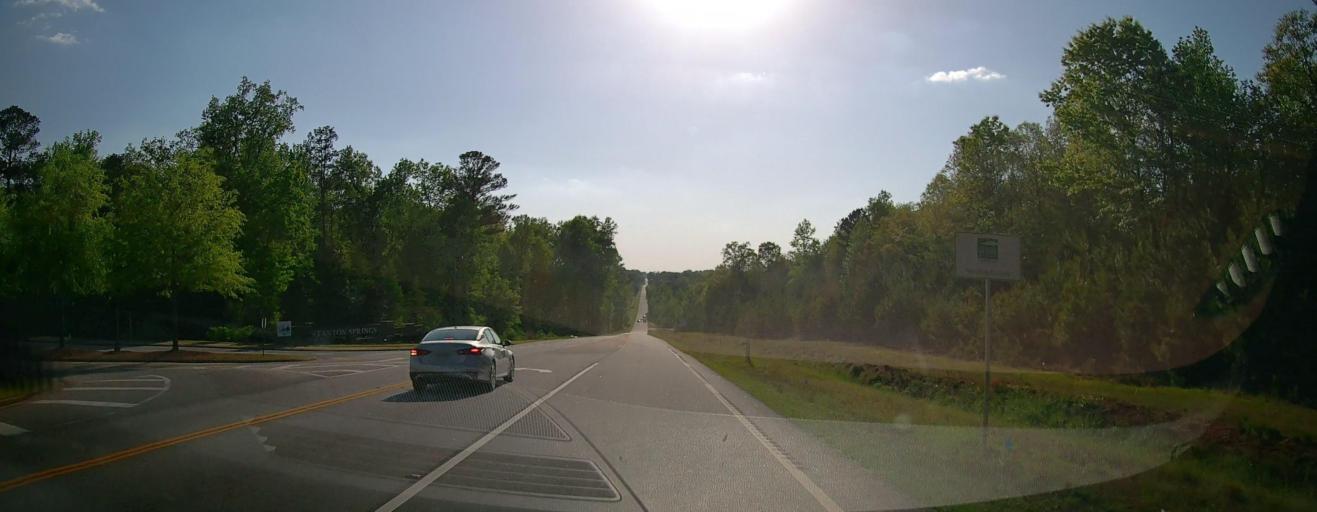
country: US
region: Georgia
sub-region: Walton County
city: Social Circle
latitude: 33.6078
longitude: -83.7031
